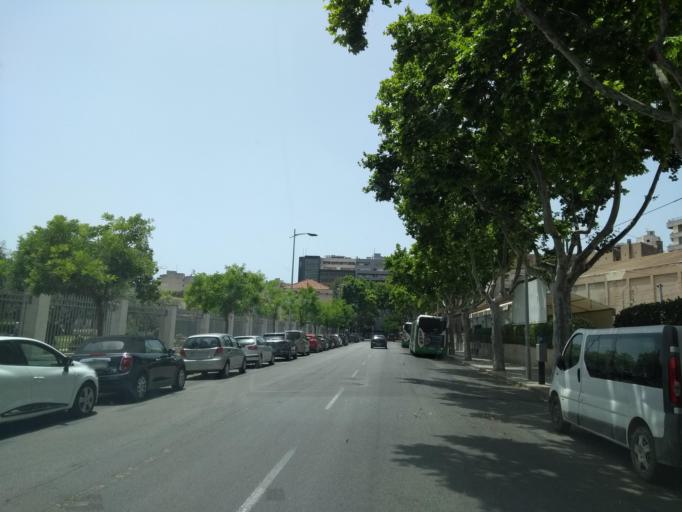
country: ES
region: Balearic Islands
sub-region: Illes Balears
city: Palma
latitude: 39.5774
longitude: 2.6551
